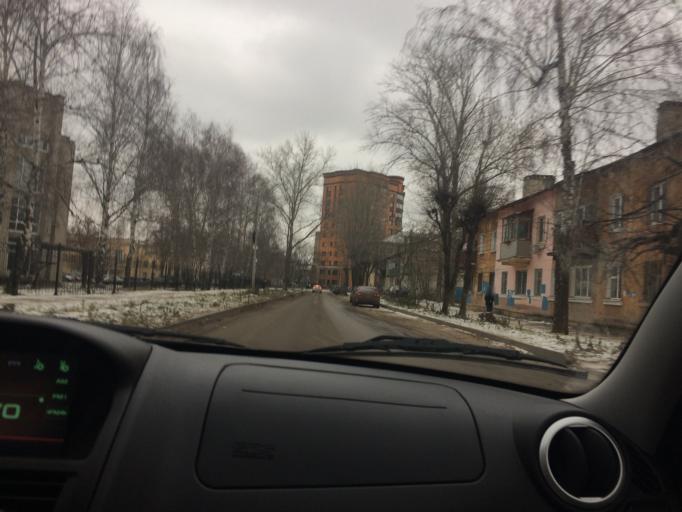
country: RU
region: Rjazan
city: Ryazan'
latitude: 54.6205
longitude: 39.7123
